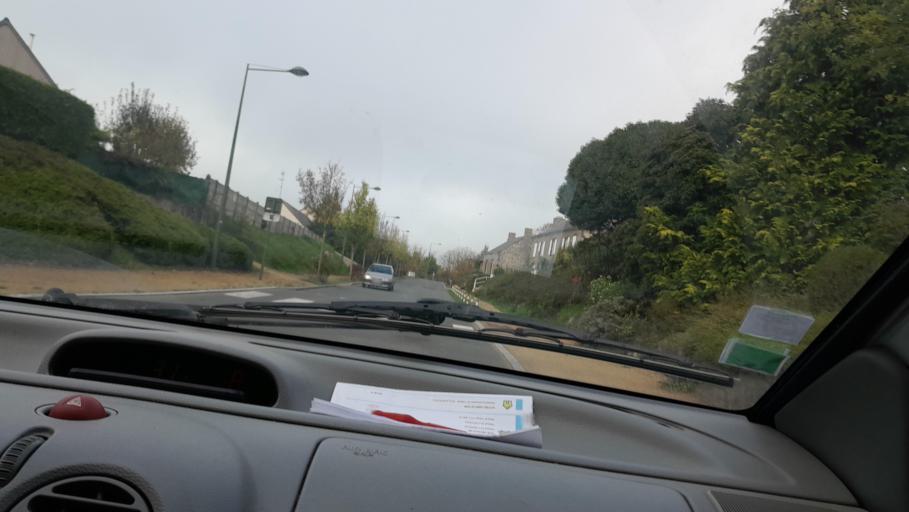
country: FR
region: Pays de la Loire
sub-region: Departement de la Mayenne
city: Juvigne
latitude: 48.2174
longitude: -1.0884
